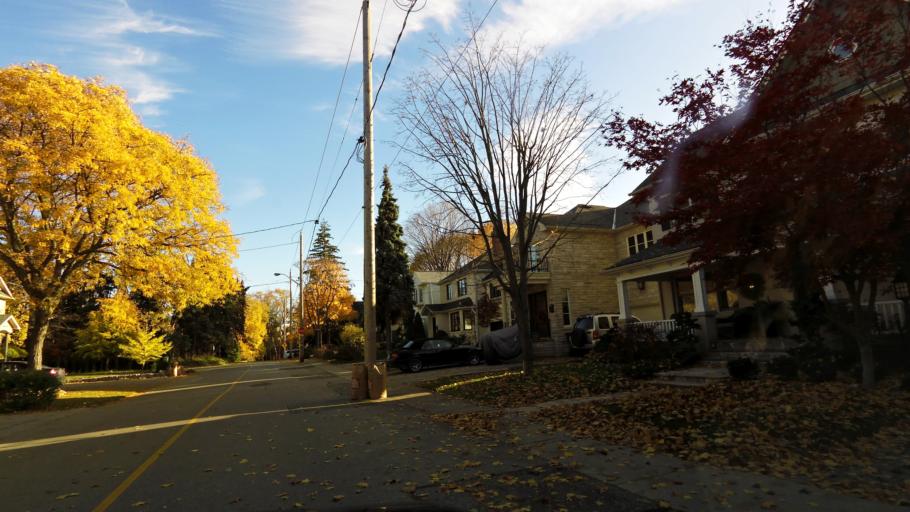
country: CA
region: Ontario
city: Etobicoke
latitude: 43.6591
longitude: -79.5038
